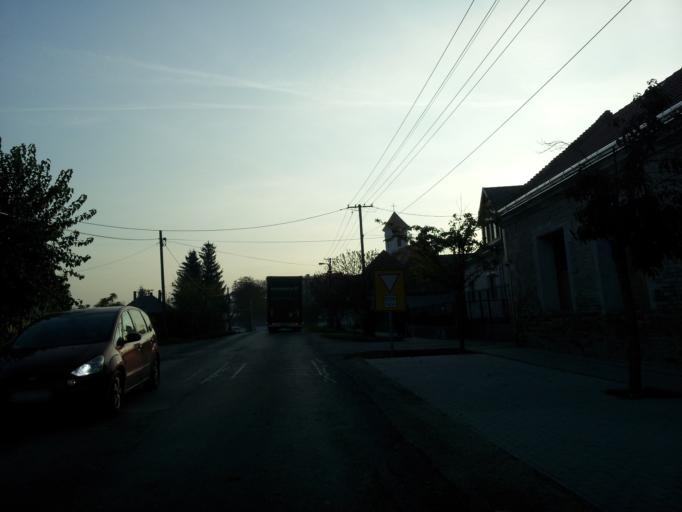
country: HU
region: Komarom-Esztergom
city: Kisber
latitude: 47.4760
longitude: 17.9592
